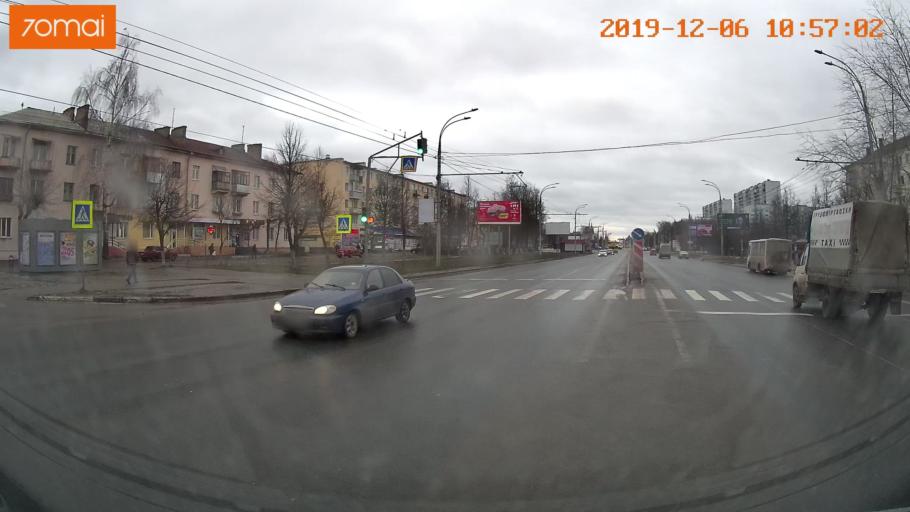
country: RU
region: Ivanovo
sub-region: Gorod Ivanovo
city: Ivanovo
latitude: 56.9672
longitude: 40.9733
